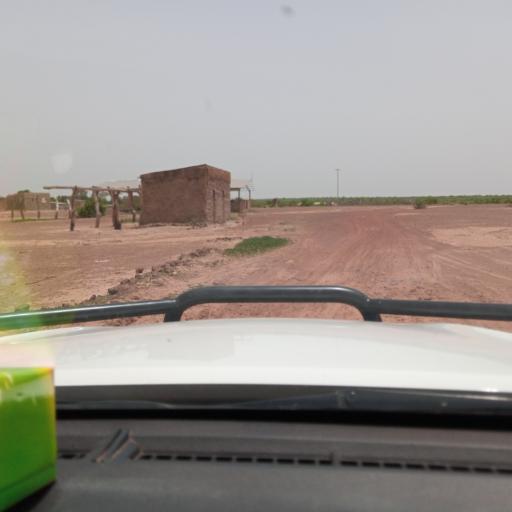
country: ML
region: Koulikoro
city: Koulikoro
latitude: 13.1086
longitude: -7.6131
